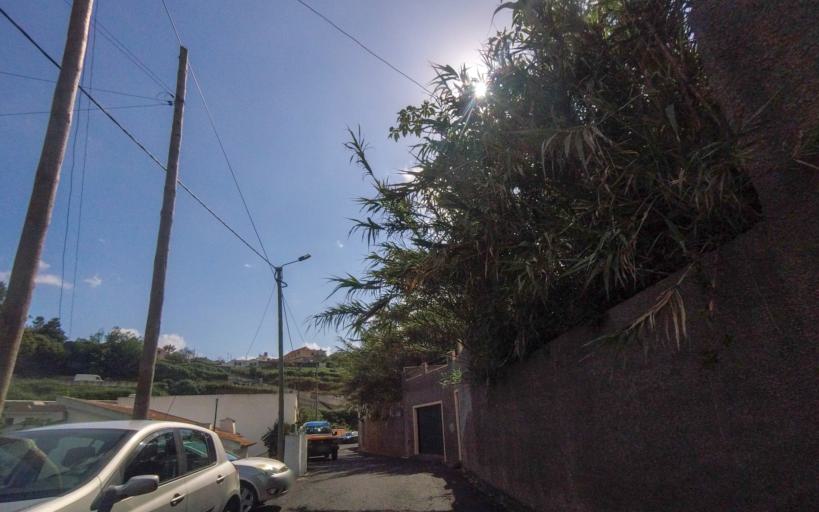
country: PT
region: Madeira
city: Camara de Lobos
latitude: 32.6742
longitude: -16.9458
